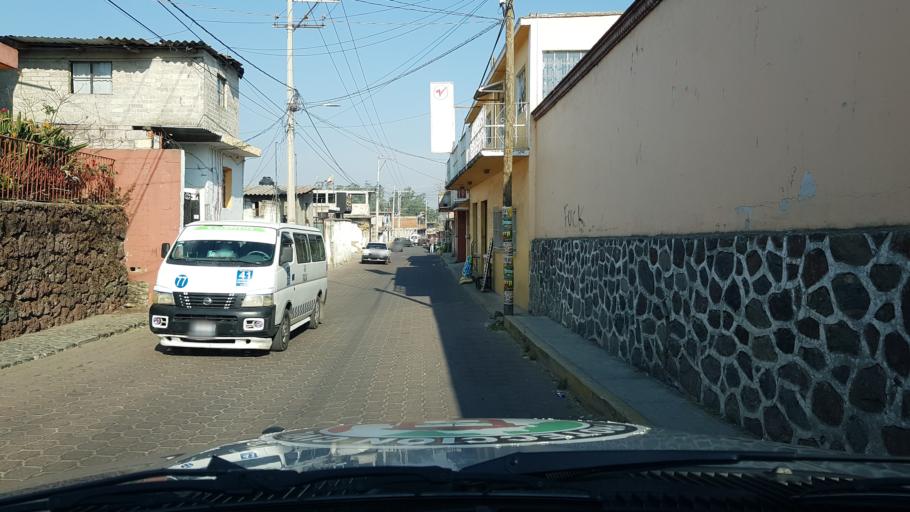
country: MX
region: Mexico
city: Ozumba de Alzate
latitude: 19.0554
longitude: -98.7713
